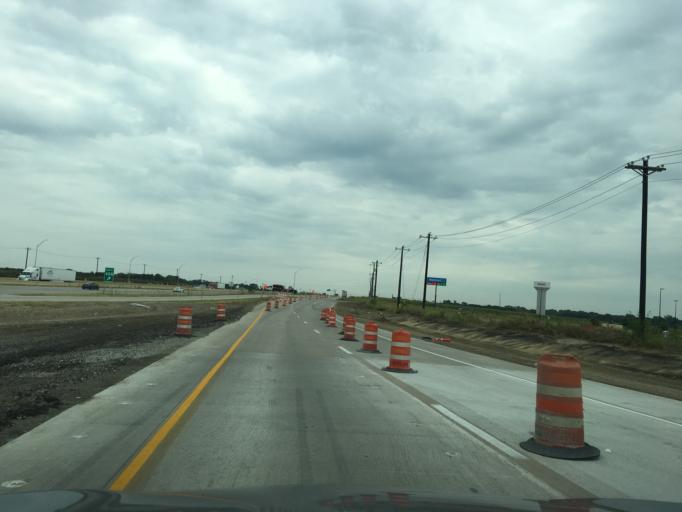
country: US
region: Texas
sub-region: Collin County
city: Anna
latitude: 33.3470
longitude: -96.5856
